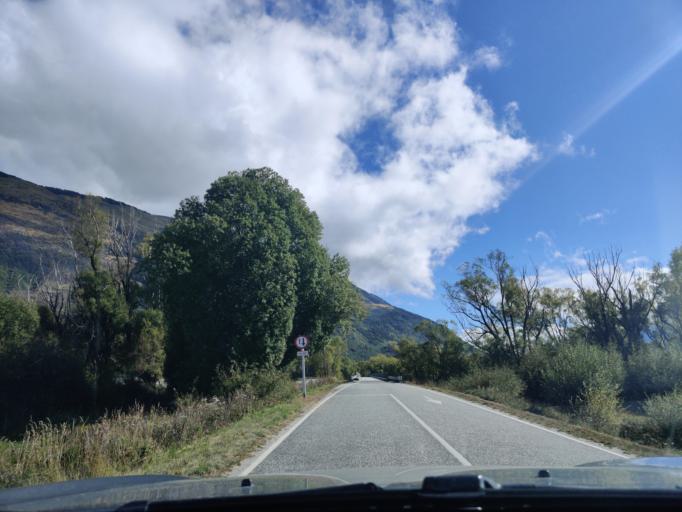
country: NZ
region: Otago
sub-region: Queenstown-Lakes District
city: Queenstown
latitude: -44.7885
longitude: 168.3978
